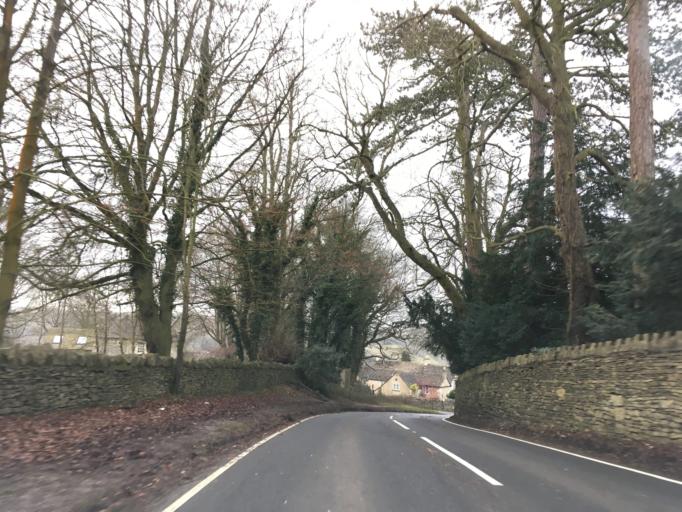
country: GB
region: England
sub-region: Gloucestershire
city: Nailsworth
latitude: 51.6992
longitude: -2.2096
